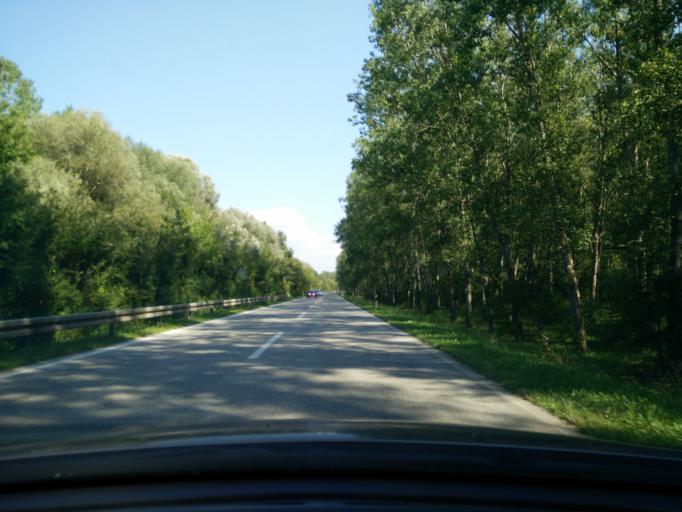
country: HR
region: Istarska
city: Karojba
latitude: 45.3516
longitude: 13.7634
